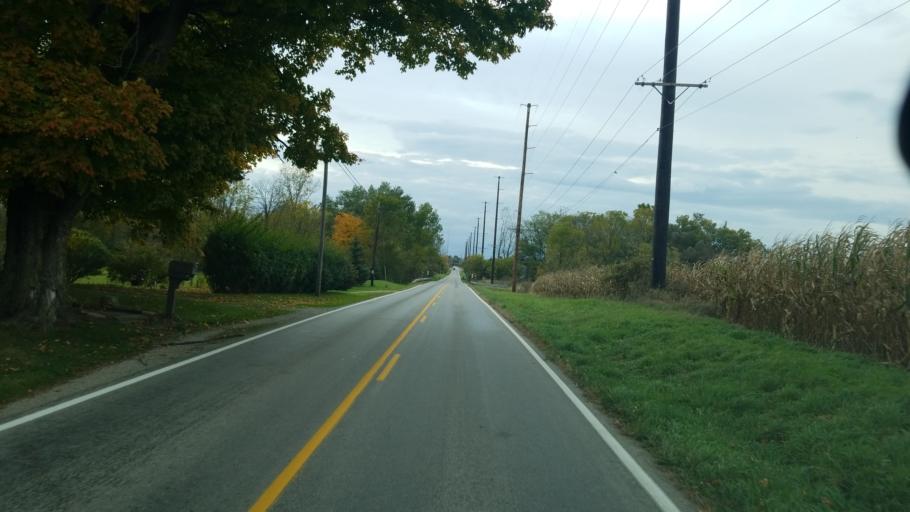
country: US
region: Ohio
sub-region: Ashland County
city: Ashland
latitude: 40.8722
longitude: -82.2800
